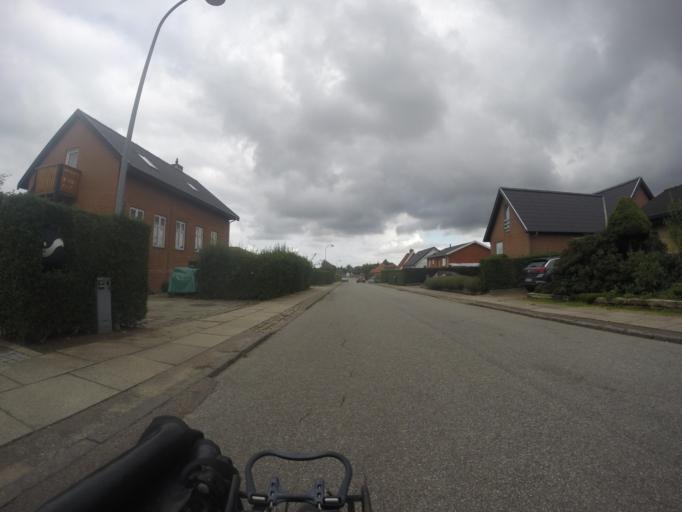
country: DK
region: Capital Region
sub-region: Herlev Kommune
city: Herlev
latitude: 55.7469
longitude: 12.4585
